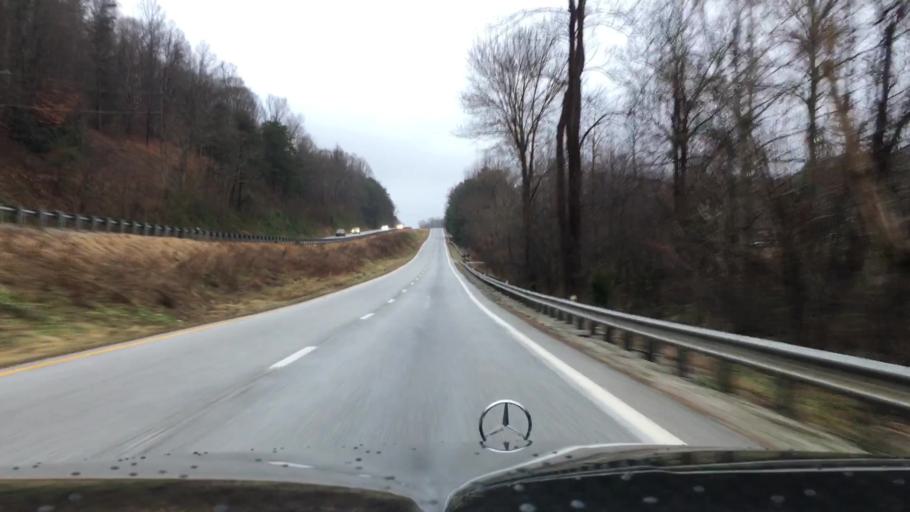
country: US
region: Virginia
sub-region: Nelson County
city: Lovingston
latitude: 37.7901
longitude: -78.8655
